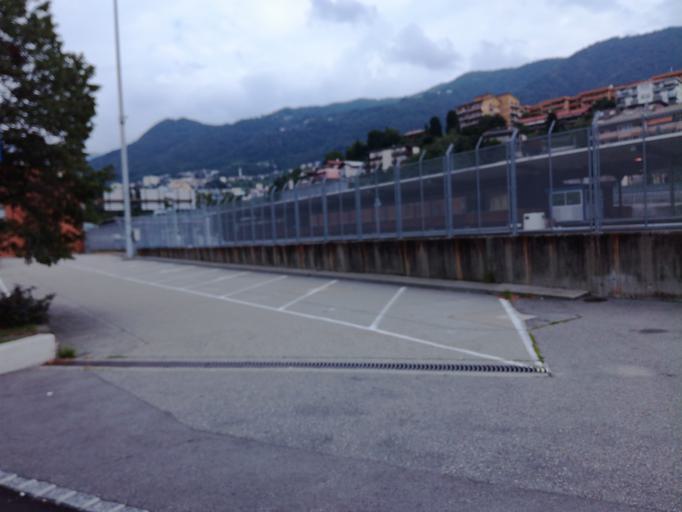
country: CH
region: Ticino
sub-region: Mendrisio District
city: Chiasso
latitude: 45.8361
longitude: 9.0361
